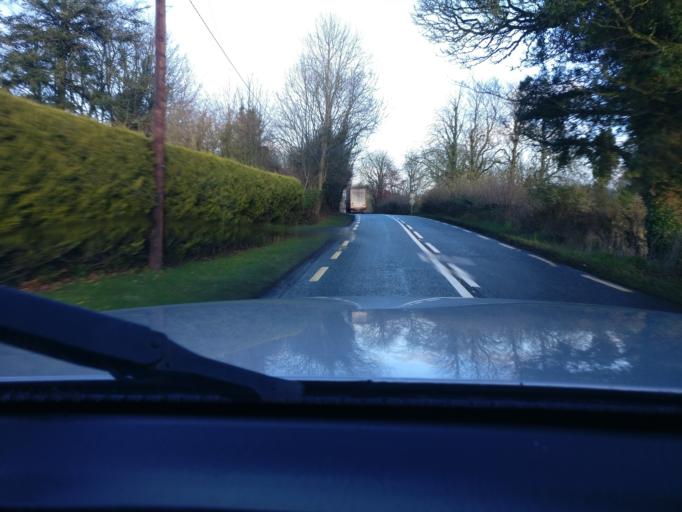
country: IE
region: Leinster
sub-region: An Mhi
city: Athboy
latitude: 53.6460
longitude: -7.0338
